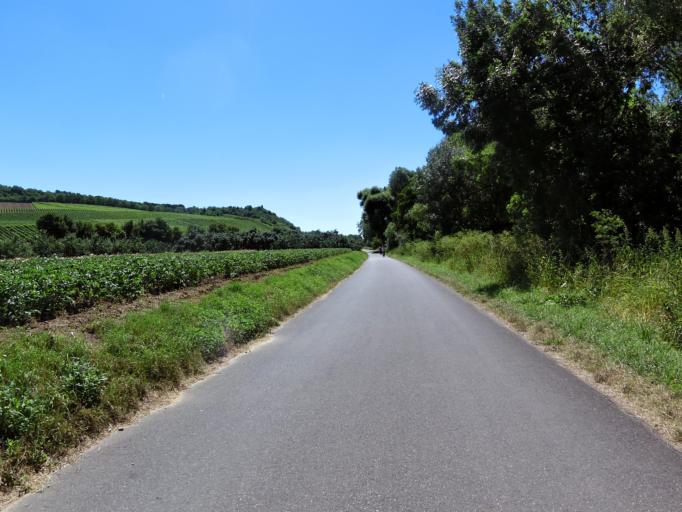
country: DE
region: Bavaria
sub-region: Regierungsbezirk Unterfranken
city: Sommerhausen
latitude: 49.6887
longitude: 10.0252
